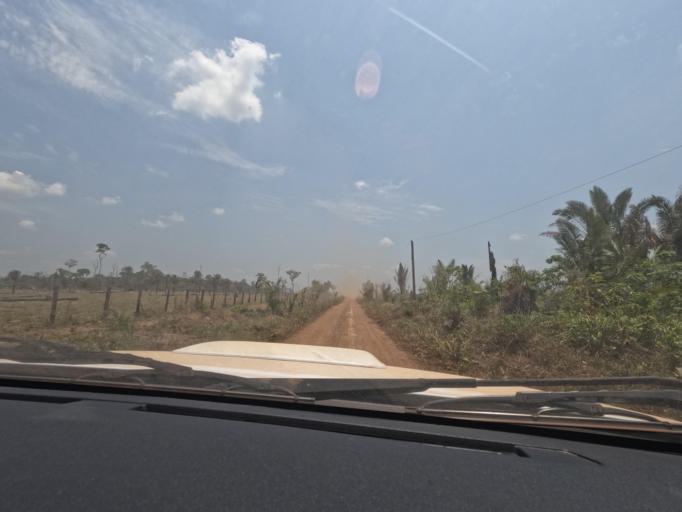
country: BR
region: Rondonia
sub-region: Porto Velho
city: Porto Velho
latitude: -8.6499
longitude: -64.1699
